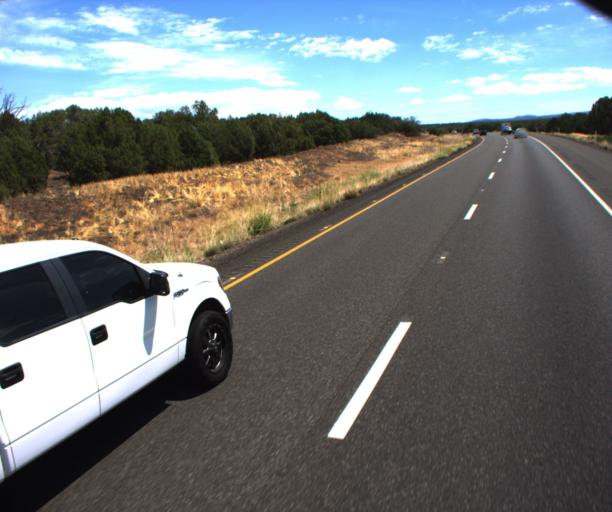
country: US
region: Arizona
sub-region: Yavapai County
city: Big Park
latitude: 34.7310
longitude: -111.7032
